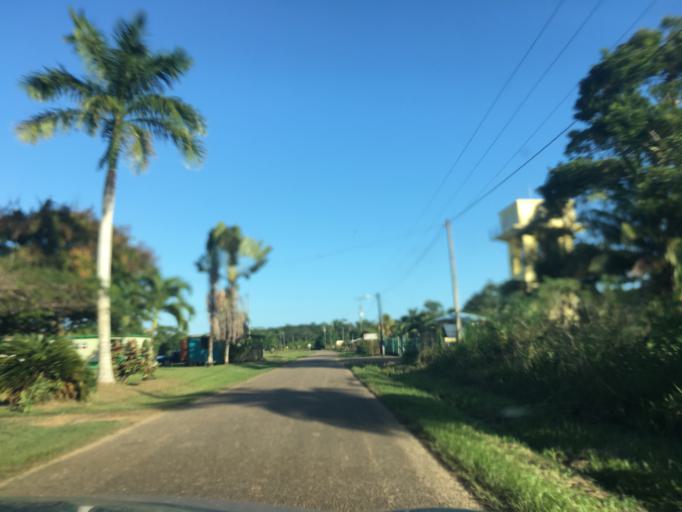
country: BZ
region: Stann Creek
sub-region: Dangriga
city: Dangriga
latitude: 16.8208
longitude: -88.3242
